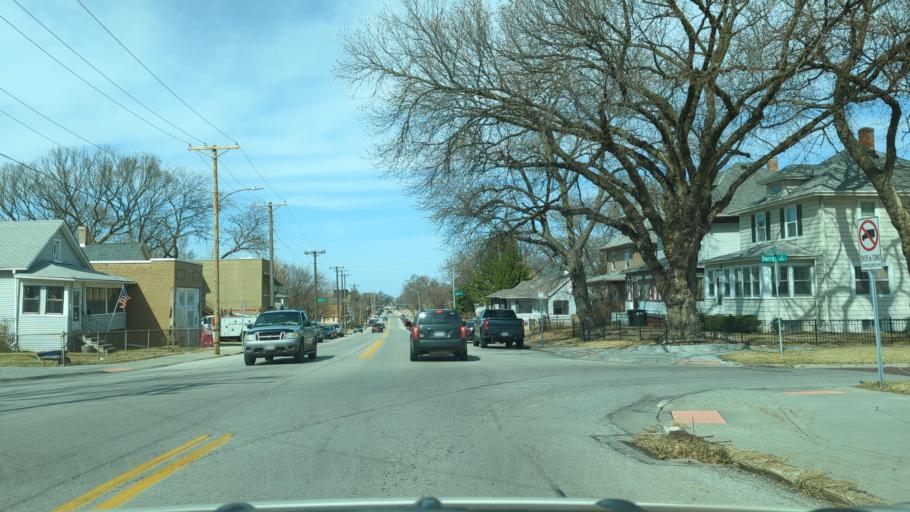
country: US
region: Nebraska
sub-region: Douglas County
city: Omaha
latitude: 41.2392
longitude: -95.9293
